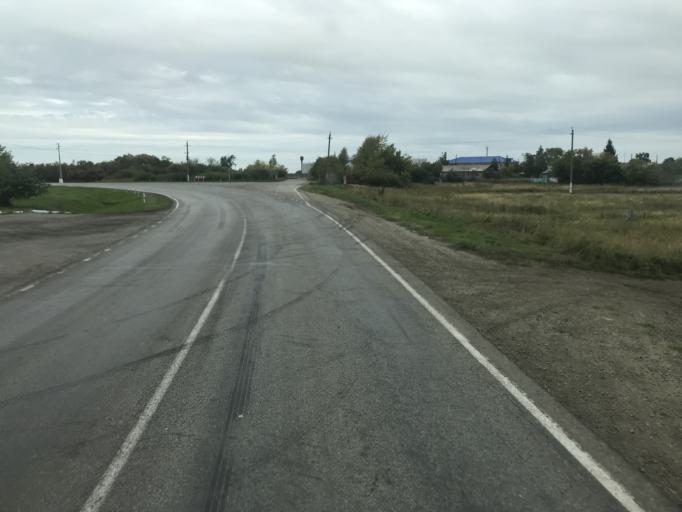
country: KZ
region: Qostanay
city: Komsomolets
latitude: 53.8750
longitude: 61.9596
